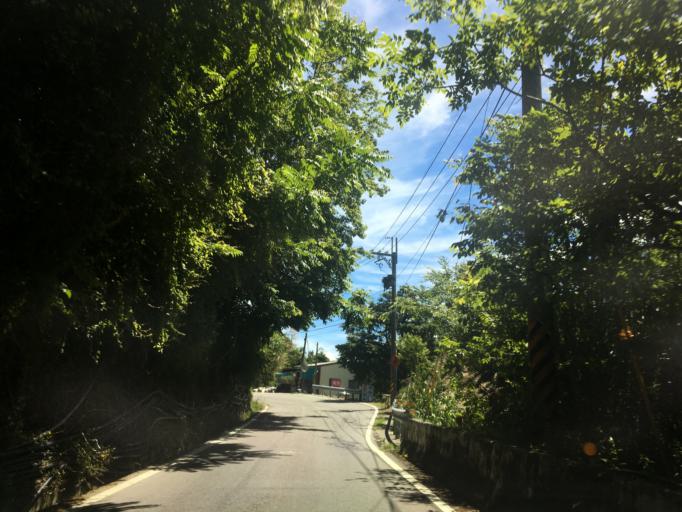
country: TW
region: Taiwan
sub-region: Nantou
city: Puli
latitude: 24.2490
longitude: 121.2552
